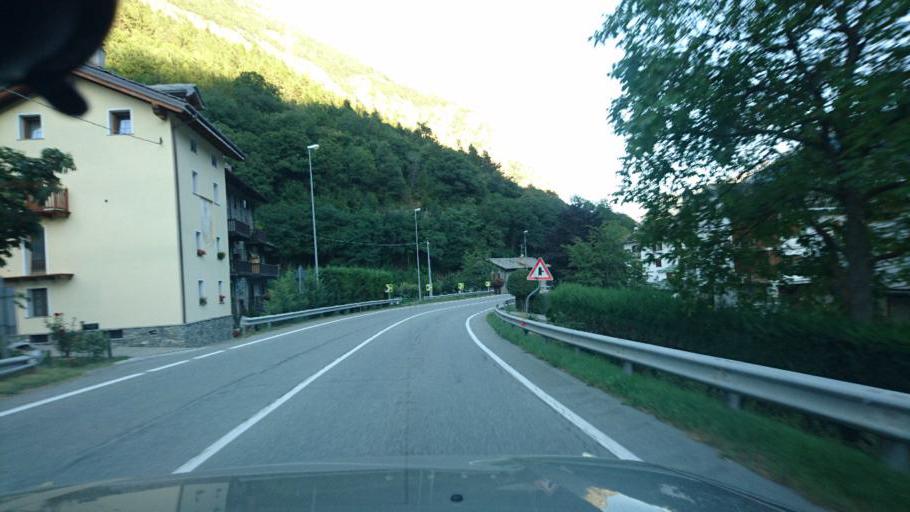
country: IT
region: Aosta Valley
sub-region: Valle d'Aosta
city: La Salle
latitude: 45.7291
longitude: 7.0885
